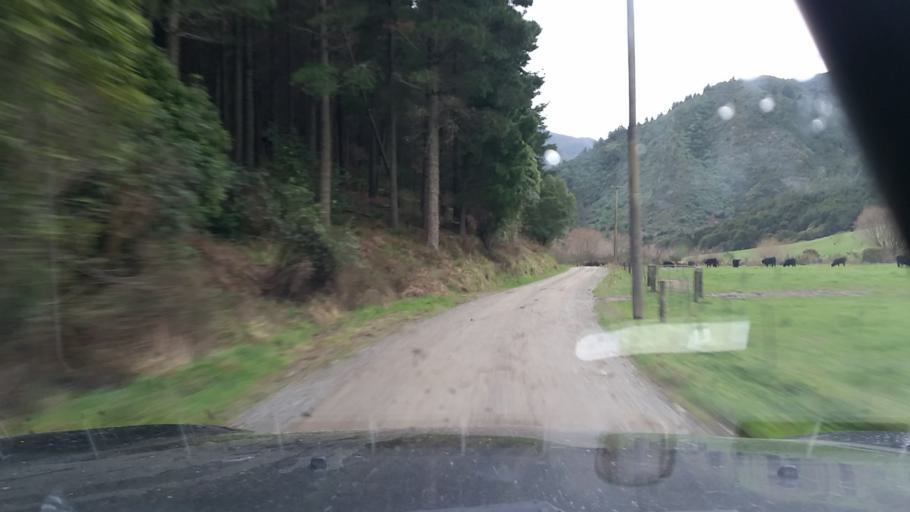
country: NZ
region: Marlborough
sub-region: Marlborough District
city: Blenheim
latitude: -41.3970
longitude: 173.8504
